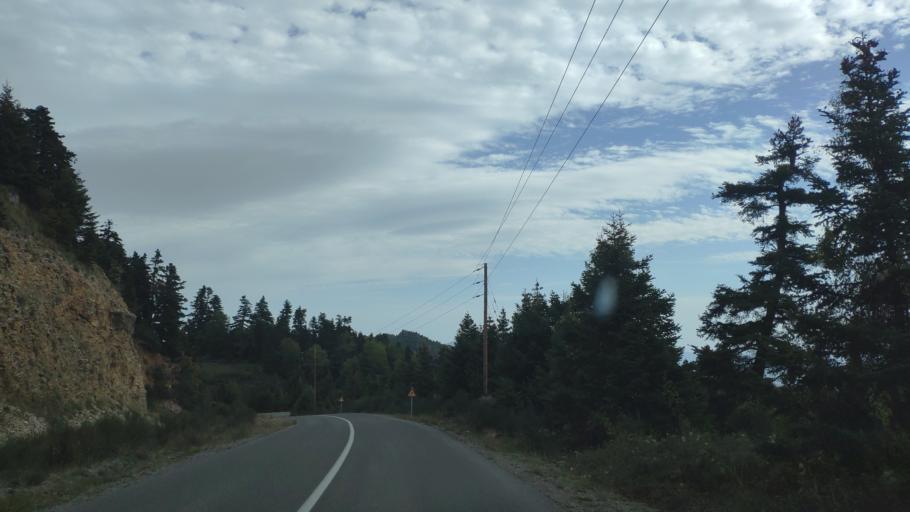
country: GR
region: Central Greece
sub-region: Nomos Fokidos
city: Amfissa
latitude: 38.7054
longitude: 22.3236
